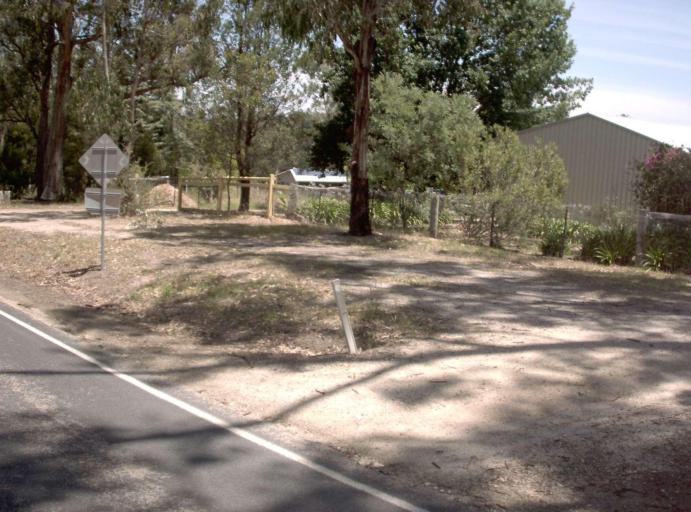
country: AU
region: Victoria
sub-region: East Gippsland
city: Lakes Entrance
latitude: -37.6903
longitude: 147.8392
